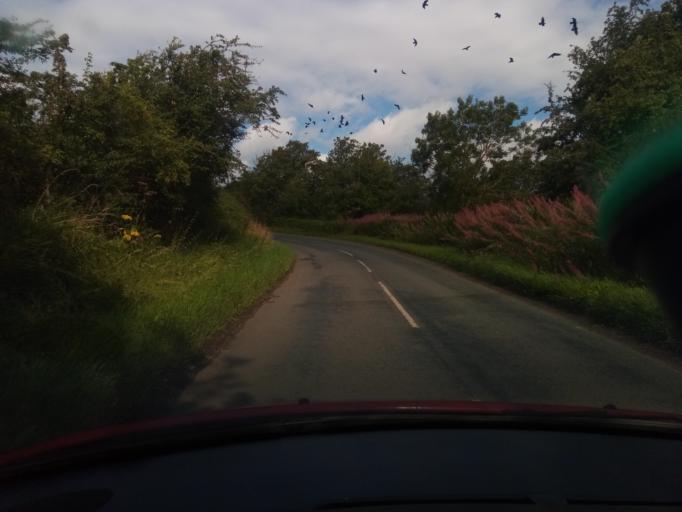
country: GB
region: Scotland
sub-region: The Scottish Borders
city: Melrose
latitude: 55.5690
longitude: -2.7283
